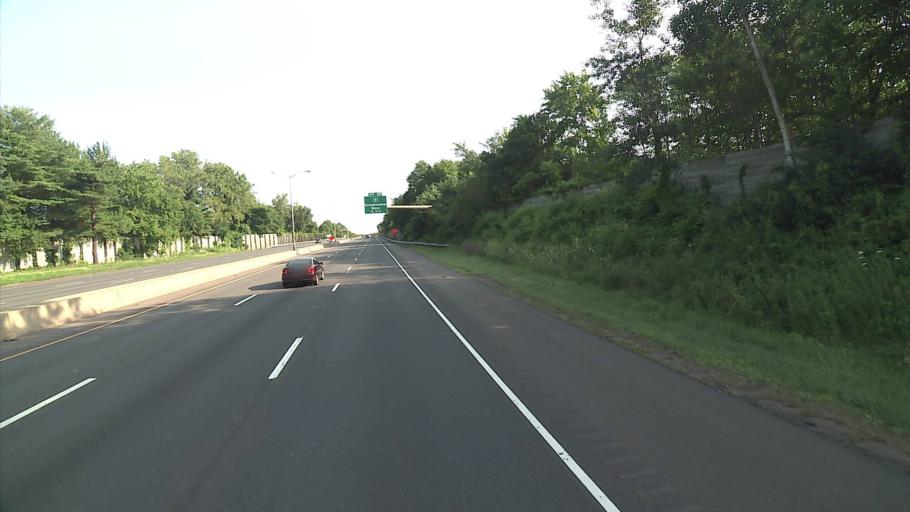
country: US
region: Connecticut
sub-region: Hartford County
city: Thompsonville
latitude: 42.0097
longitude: -72.5857
